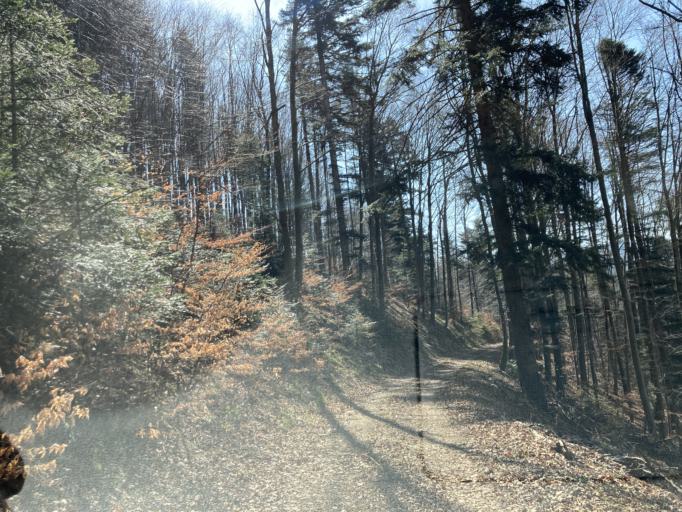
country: DE
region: Baden-Wuerttemberg
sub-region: Freiburg Region
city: Glottertal
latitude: 48.0566
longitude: 7.9768
